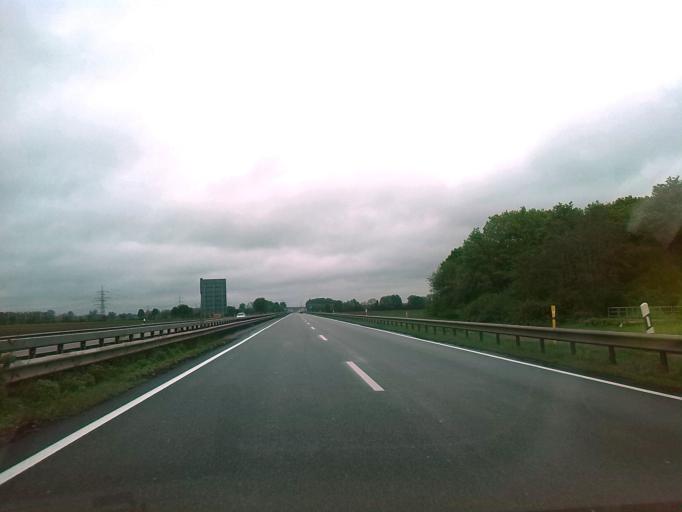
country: DE
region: Rheinland-Pfalz
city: Frankenthal
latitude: 49.5553
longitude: 8.3969
